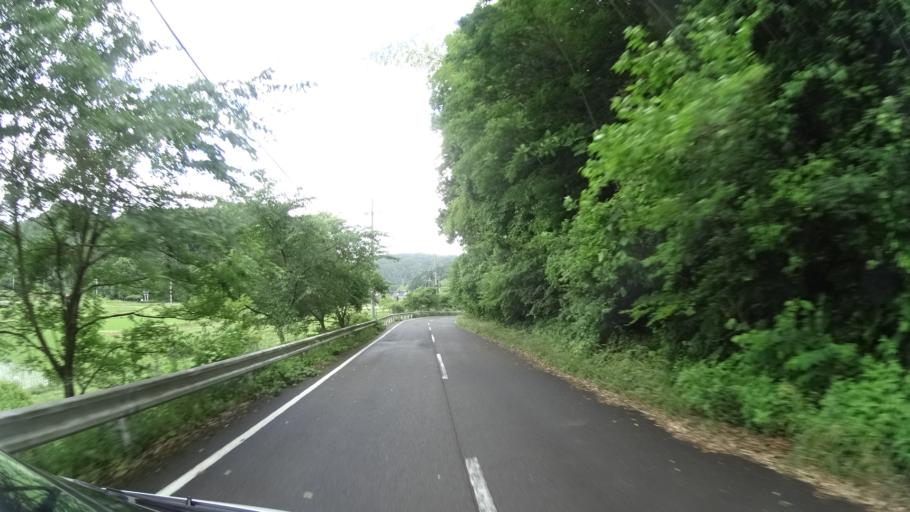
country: JP
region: Kyoto
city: Ayabe
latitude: 35.3823
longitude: 135.2134
